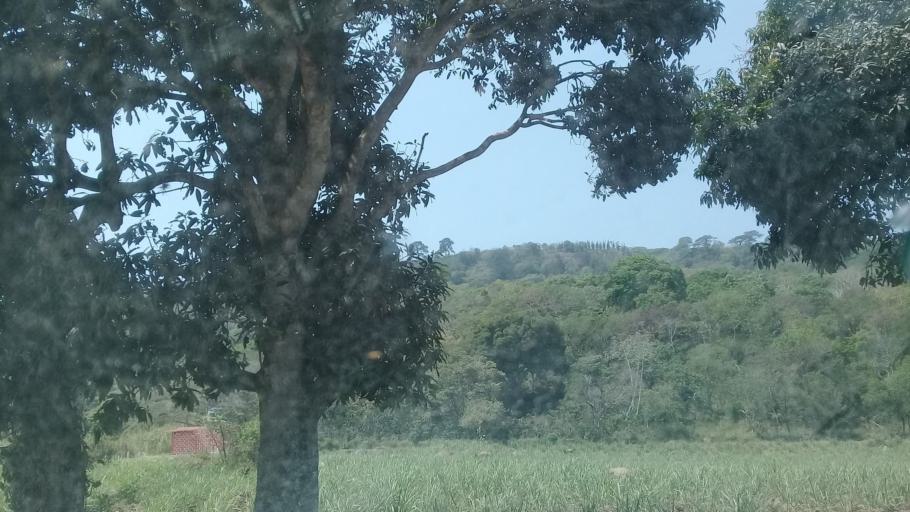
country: MX
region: Veracruz
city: El Castillo
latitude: 19.5650
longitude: -96.8441
